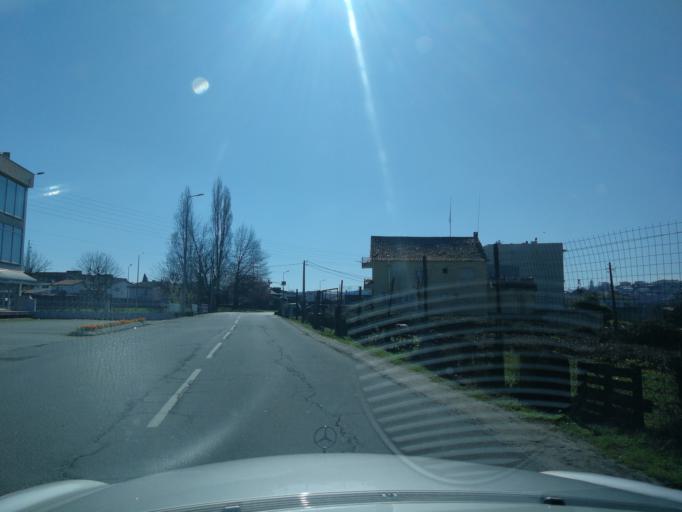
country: PT
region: Braga
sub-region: Vila Nova de Famalicao
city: Calendario
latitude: 41.3970
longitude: -8.5209
